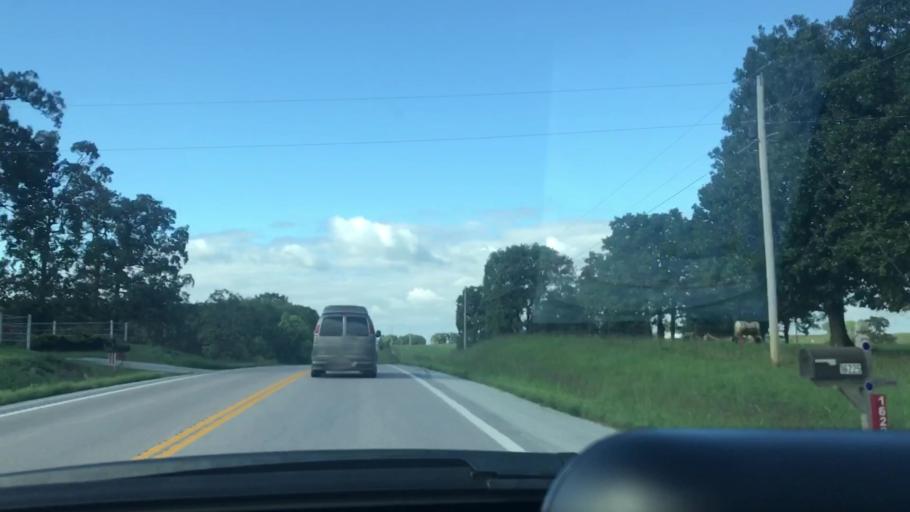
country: US
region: Missouri
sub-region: Hickory County
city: Hermitage
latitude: 37.9736
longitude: -93.2062
